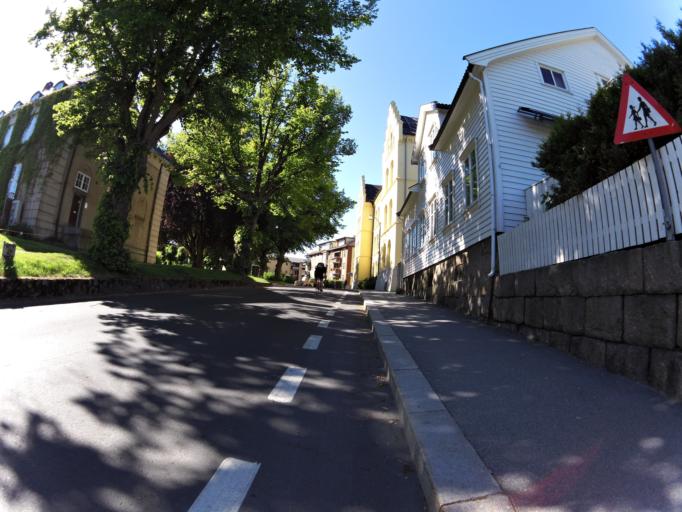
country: NO
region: Ostfold
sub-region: Fredrikstad
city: Fredrikstad
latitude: 59.2065
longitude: 10.9515
